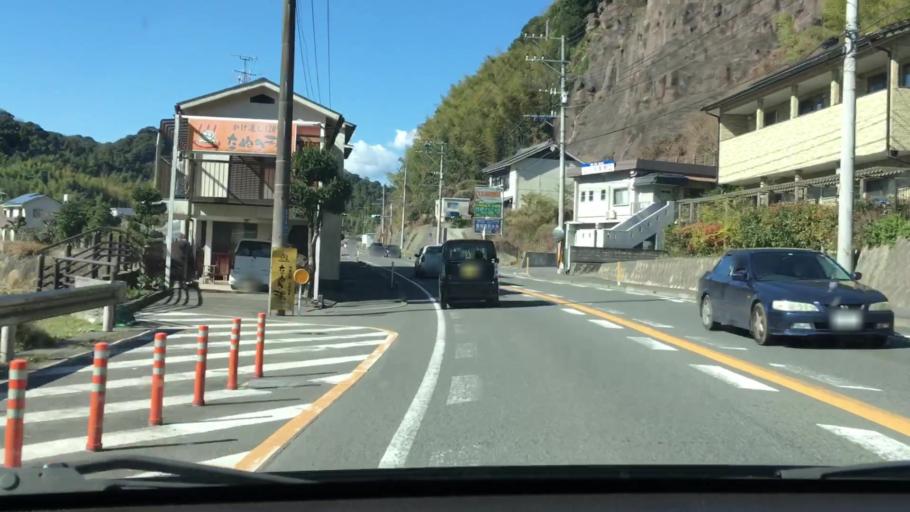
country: JP
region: Kagoshima
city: Kagoshima-shi
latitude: 31.6342
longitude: 130.5229
